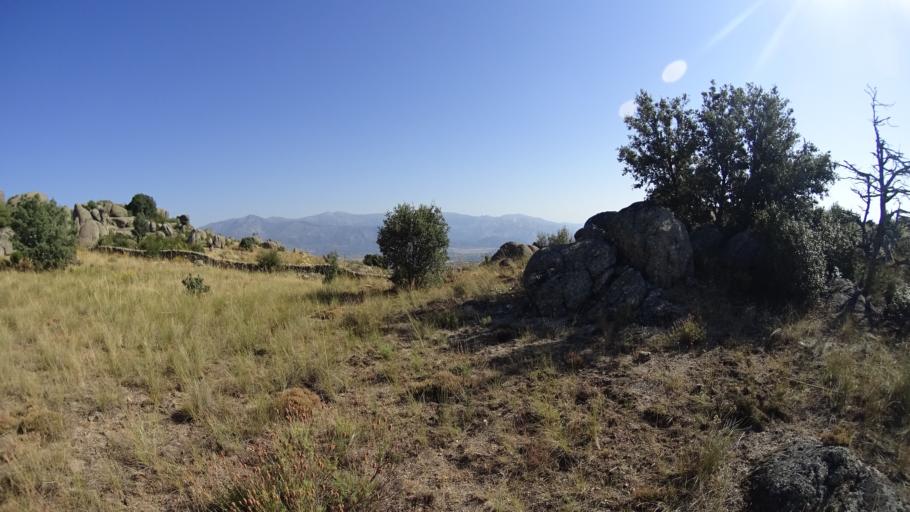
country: ES
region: Madrid
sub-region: Provincia de Madrid
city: Moralzarzal
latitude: 40.6506
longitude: -3.9451
